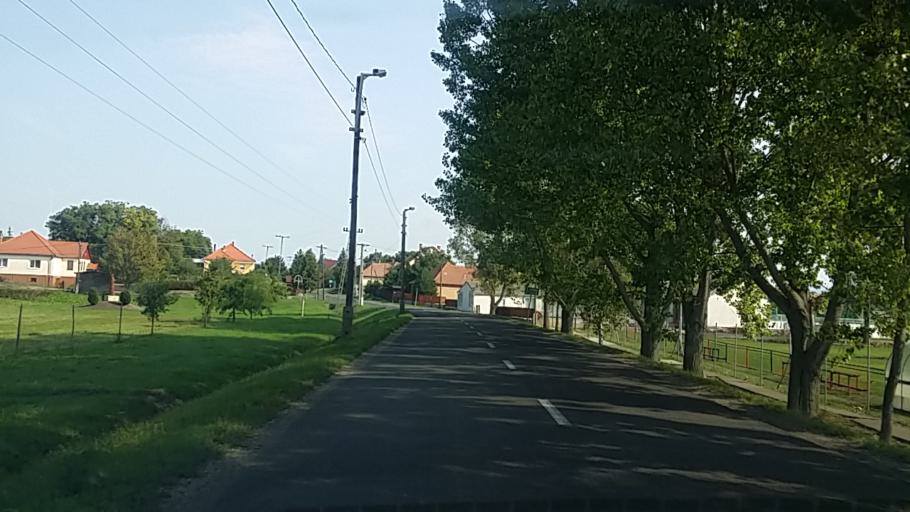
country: HU
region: Nograd
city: Hehalom
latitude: 47.7784
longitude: 19.5845
